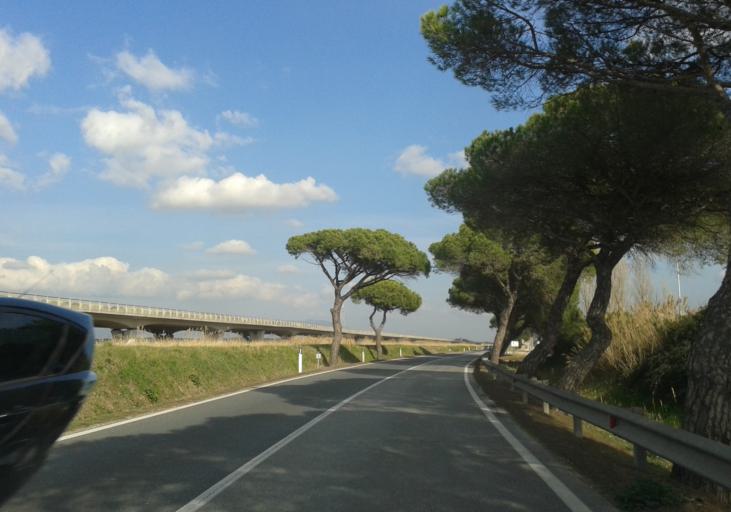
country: IT
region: Tuscany
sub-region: Provincia di Livorno
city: Guasticce
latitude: 43.6087
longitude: 10.3768
